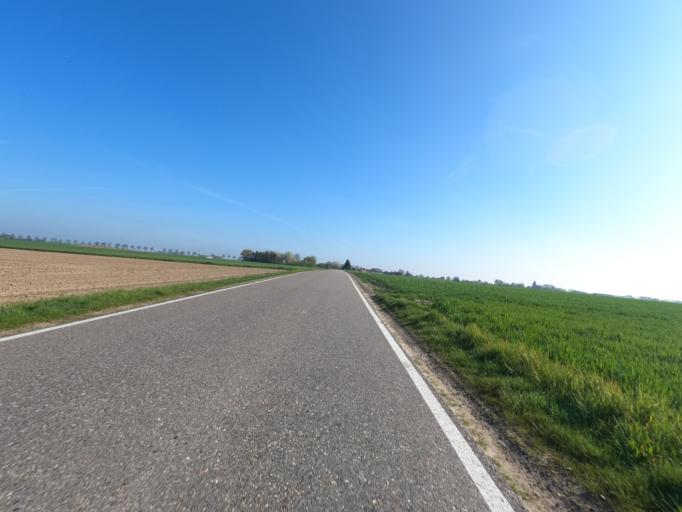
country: DE
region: North Rhine-Westphalia
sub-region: Regierungsbezirk Koln
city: Heinsberg
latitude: 51.0342
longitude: 6.0447
